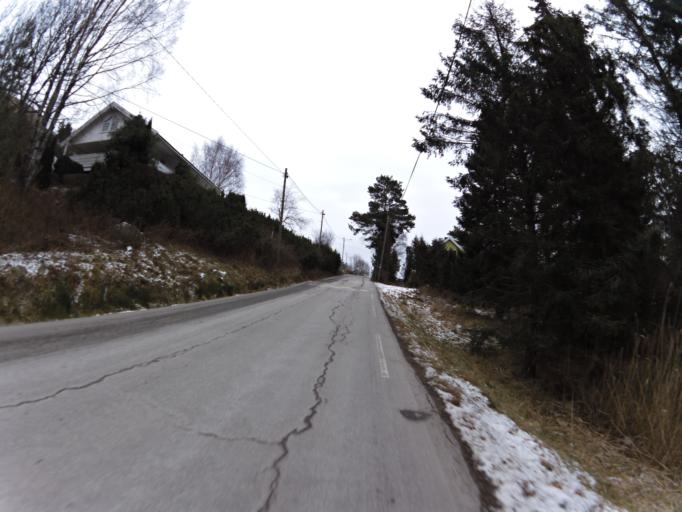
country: NO
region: Ostfold
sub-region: Fredrikstad
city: Fredrikstad
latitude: 59.2118
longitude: 10.8887
